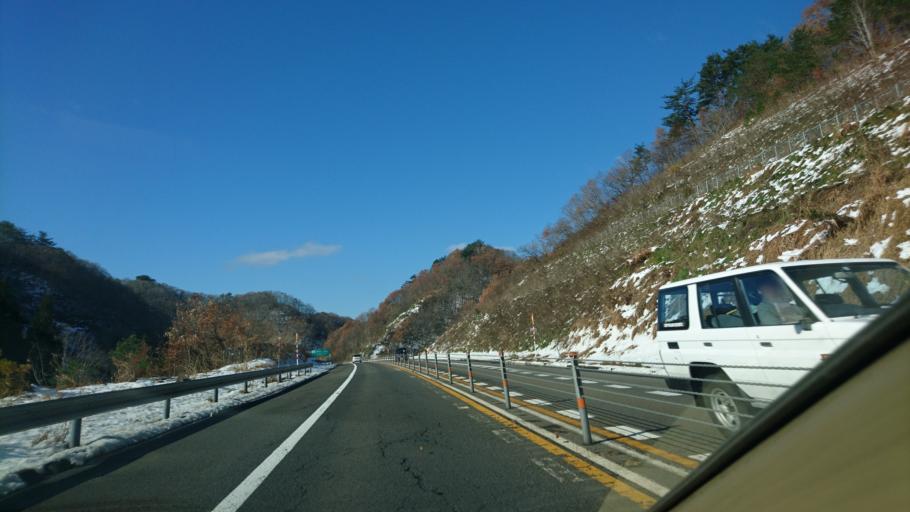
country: JP
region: Akita
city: Yokotemachi
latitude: 39.3132
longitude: 140.7716
